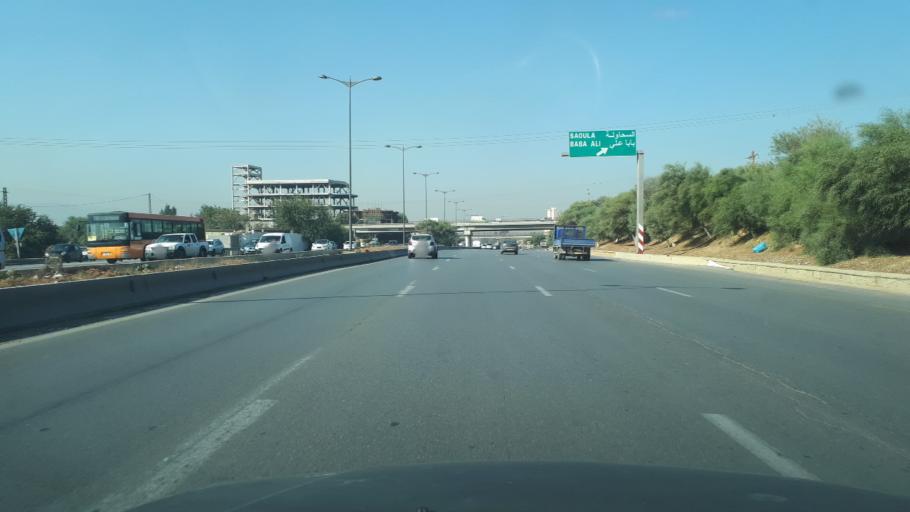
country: DZ
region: Alger
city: Birkhadem
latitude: 36.6737
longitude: 3.0530
